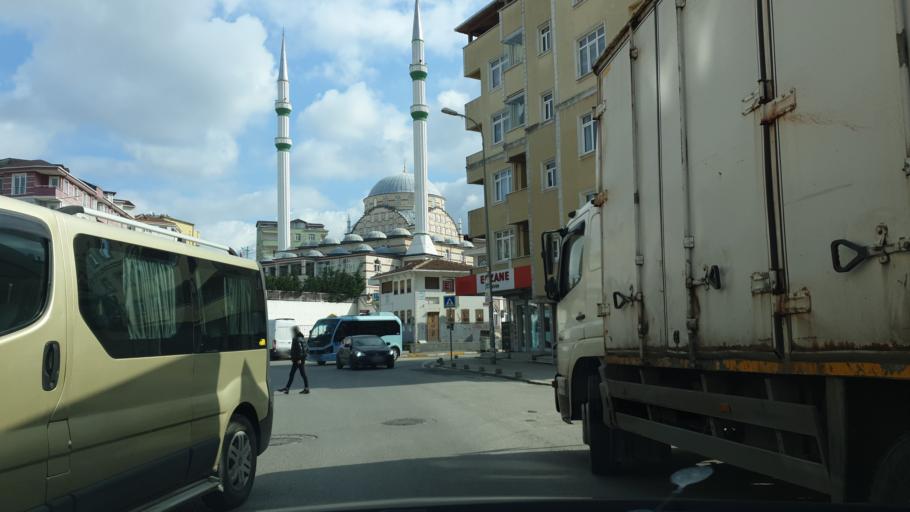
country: TR
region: Istanbul
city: Icmeler
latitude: 40.8675
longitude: 29.3027
